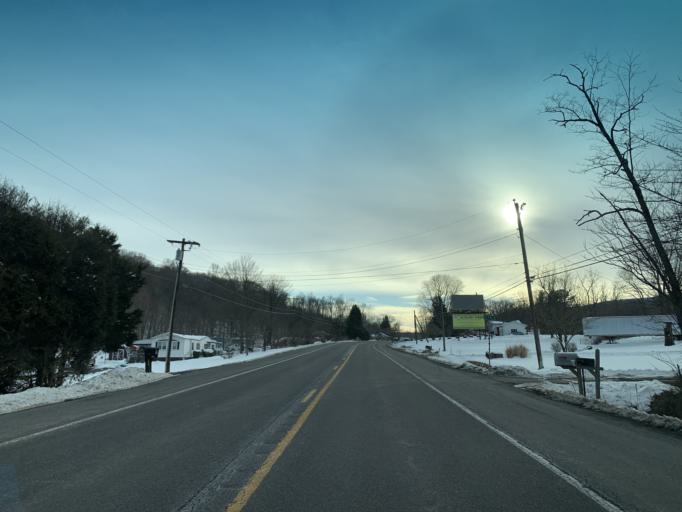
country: US
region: Maryland
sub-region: Allegany County
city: Lonaconing
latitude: 39.5153
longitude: -78.9154
